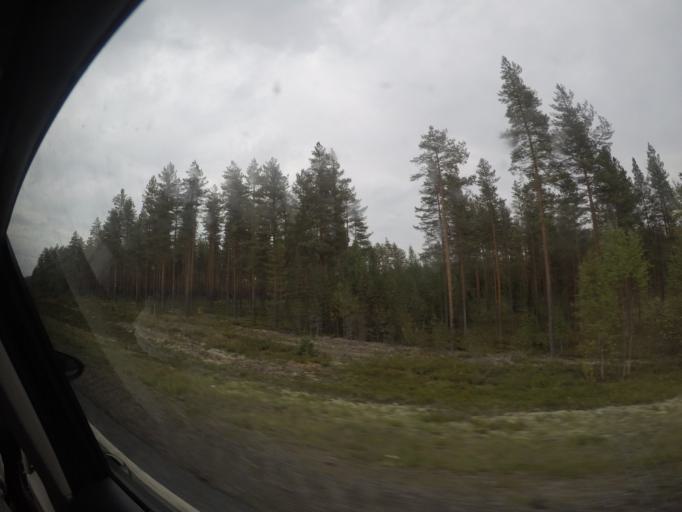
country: FI
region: Pirkanmaa
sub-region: Ylae-Pirkanmaa
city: Juupajoki
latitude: 61.7861
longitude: 24.2998
